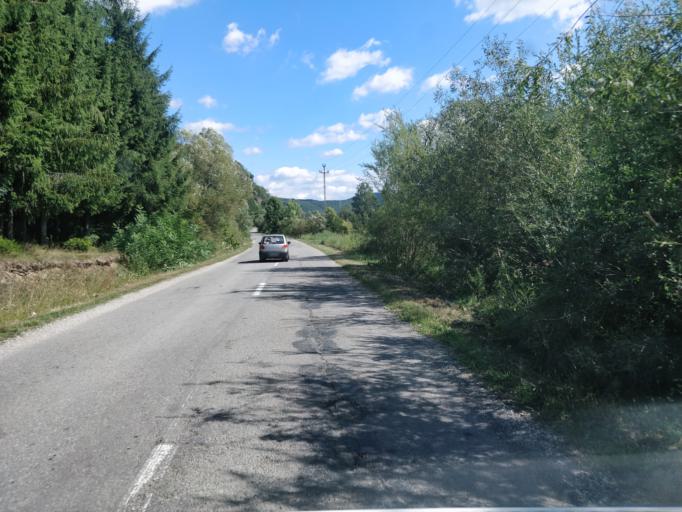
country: RO
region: Cluj
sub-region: Comuna Sacueu
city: Sacuieu
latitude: 46.8689
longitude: 22.8746
